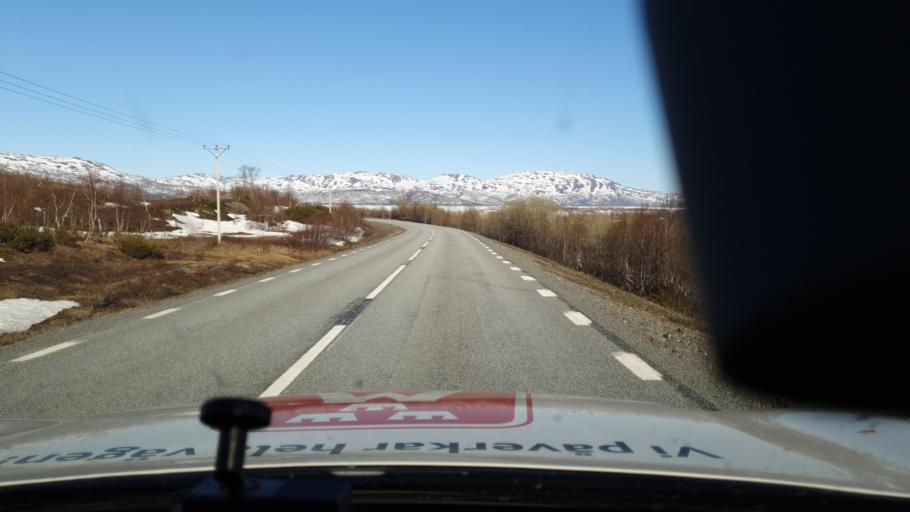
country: NO
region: Nordland
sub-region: Rana
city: Mo i Rana
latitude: 66.1212
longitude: 14.6931
